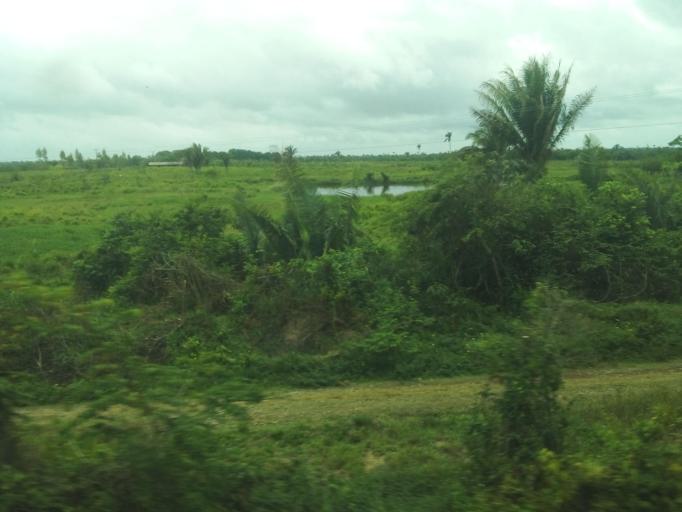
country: BR
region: Maranhao
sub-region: Moncao
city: Moncao
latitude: -3.5826
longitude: -45.0611
